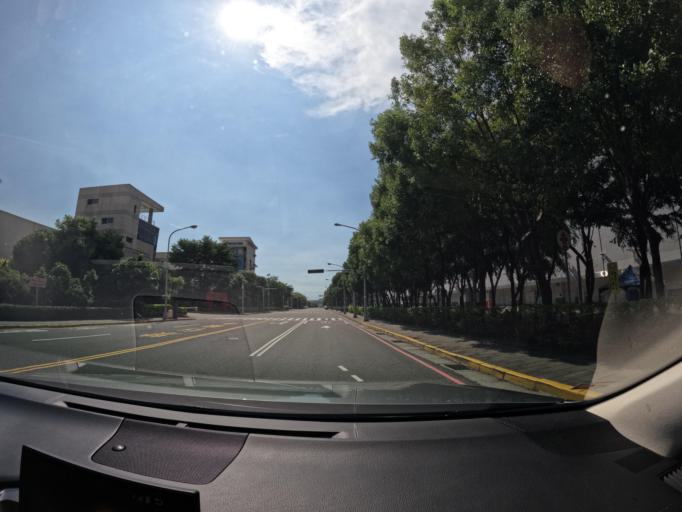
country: TW
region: Taiwan
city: Fengyuan
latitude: 24.3168
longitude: 120.7232
